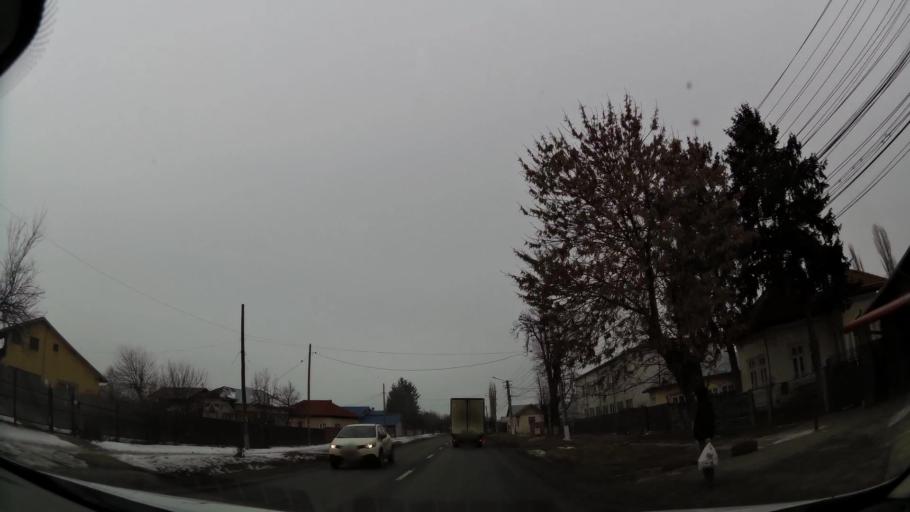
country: RO
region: Dambovita
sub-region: Comuna Racari
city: Racari
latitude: 44.6299
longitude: 25.7316
